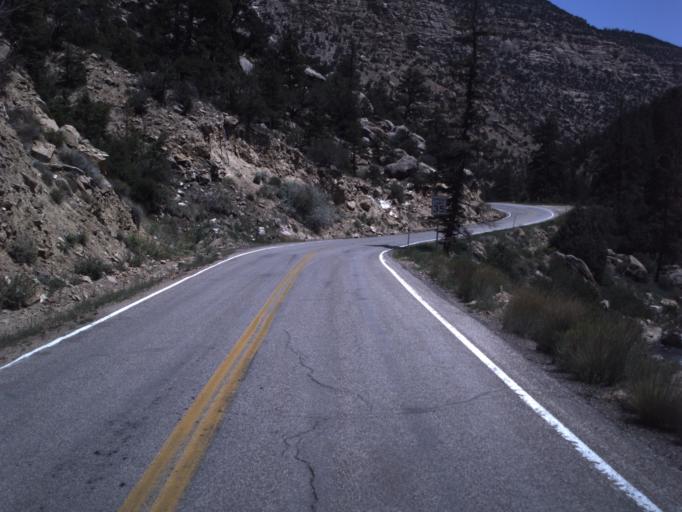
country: US
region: Utah
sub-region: Emery County
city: Orangeville
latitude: 39.2884
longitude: -111.2482
